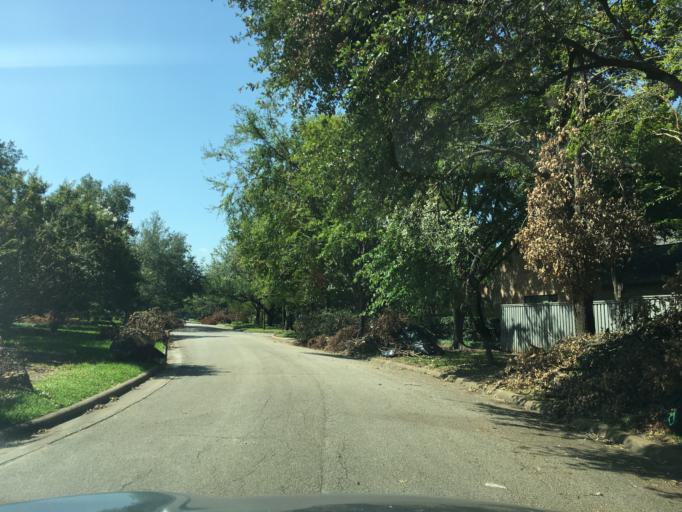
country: US
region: Texas
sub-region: Dallas County
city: Richardson
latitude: 32.9088
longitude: -96.7756
